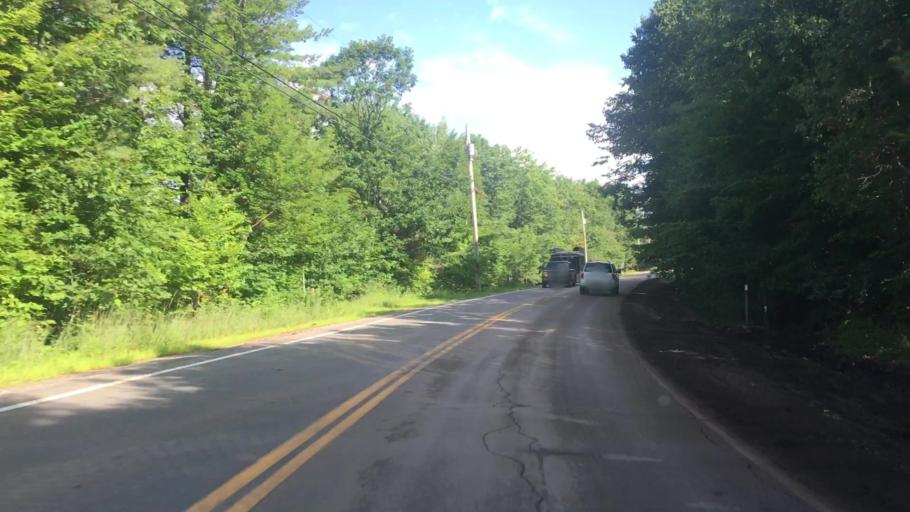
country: US
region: New Hampshire
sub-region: Belknap County
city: Gilford
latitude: 43.5303
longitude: -71.3459
